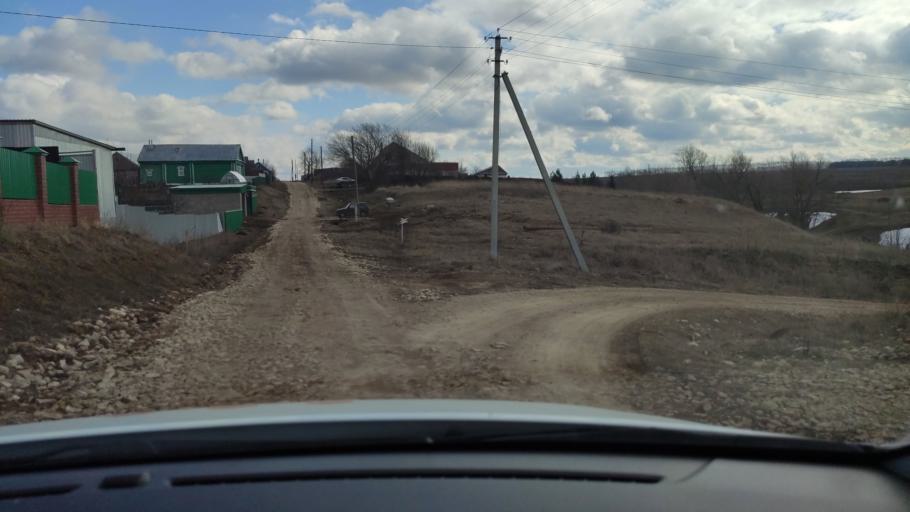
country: RU
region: Tatarstan
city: Vysokaya Gora
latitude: 56.2091
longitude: 49.3150
